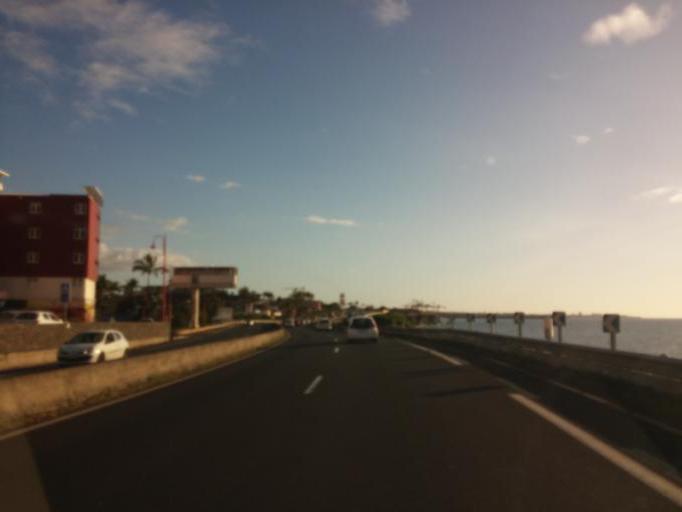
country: RE
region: Reunion
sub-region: Reunion
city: La Possession
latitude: -20.9247
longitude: 55.3390
